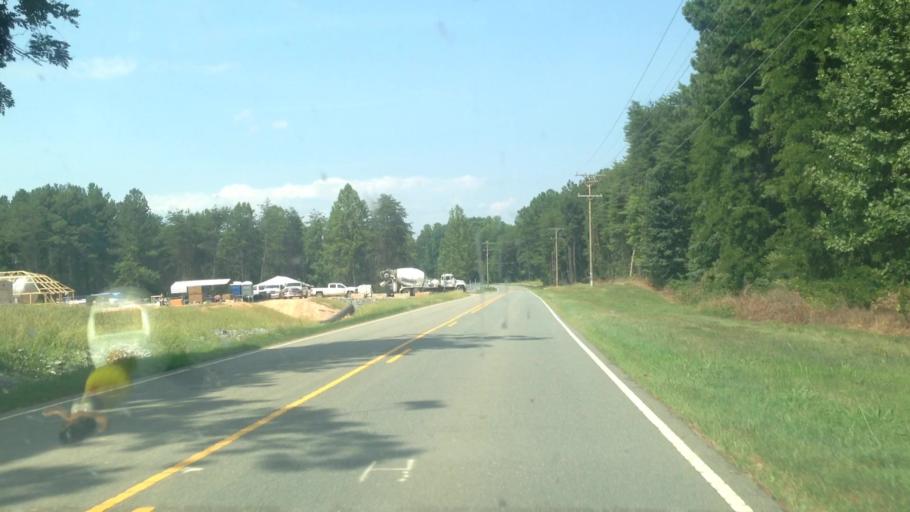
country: US
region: North Carolina
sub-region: Stokes County
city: Walnut Cove
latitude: 36.2936
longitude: -80.0634
